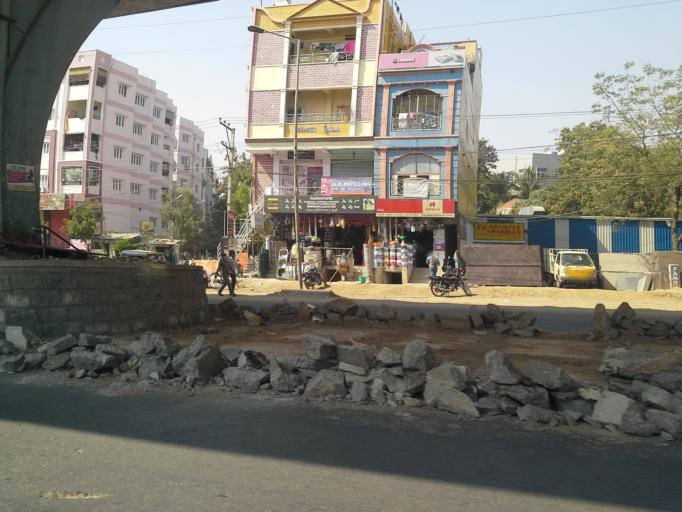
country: IN
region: Telangana
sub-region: Hyderabad
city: Hyderabad
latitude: 17.3546
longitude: 78.4209
